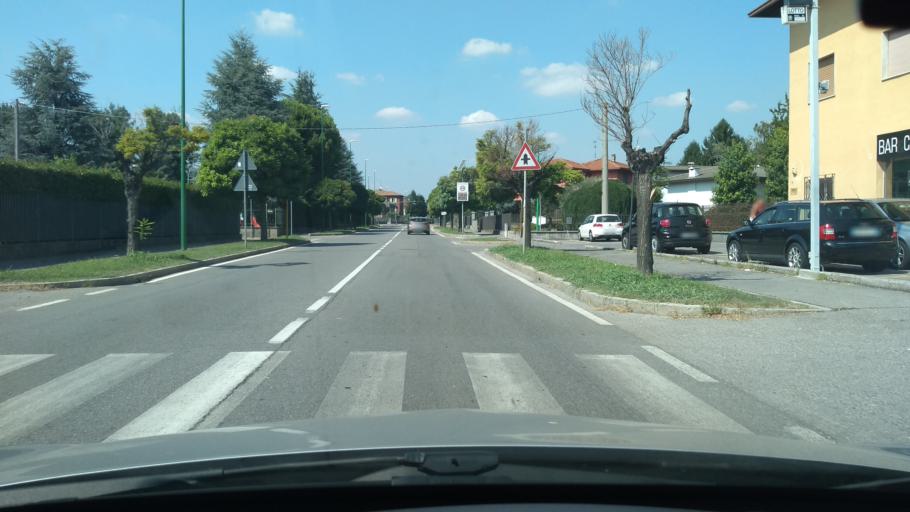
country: IT
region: Lombardy
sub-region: Provincia di Bergamo
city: Ghisalba
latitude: 45.5920
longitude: 9.7577
